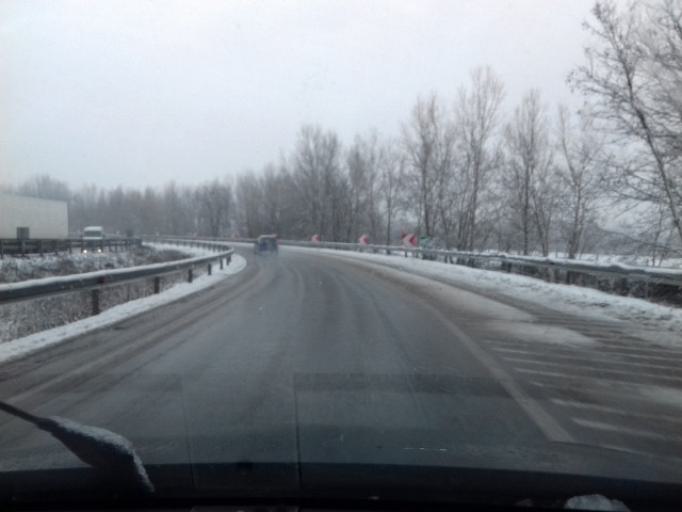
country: HU
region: Budapest
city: Budapest XV. keruelet
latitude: 47.5965
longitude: 19.1323
